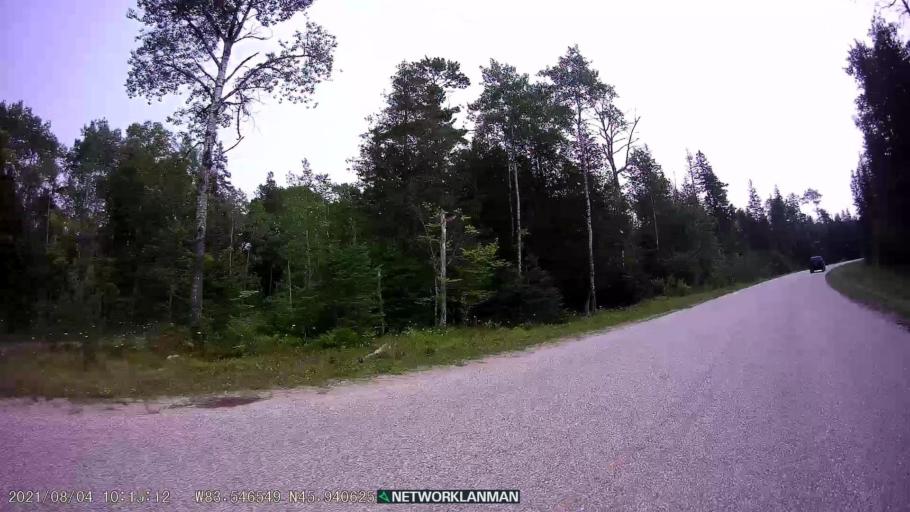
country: CA
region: Ontario
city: Thessalon
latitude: 45.9405
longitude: -83.5462
